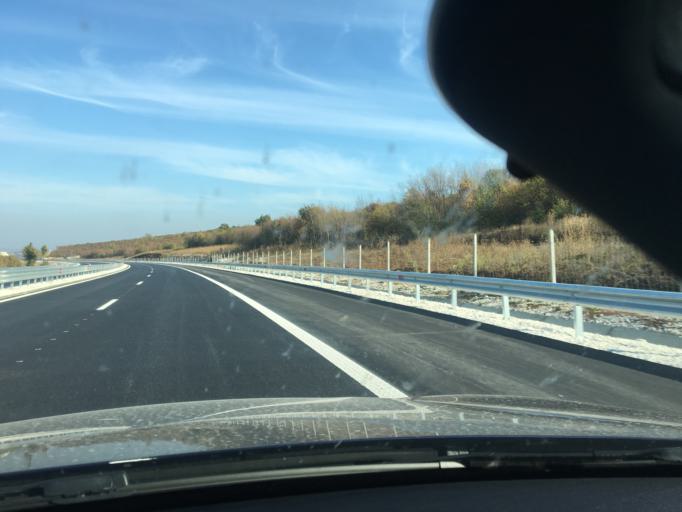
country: BG
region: Lovech
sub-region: Obshtina Yablanitsa
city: Yablanitsa
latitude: 43.0495
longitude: 24.1507
